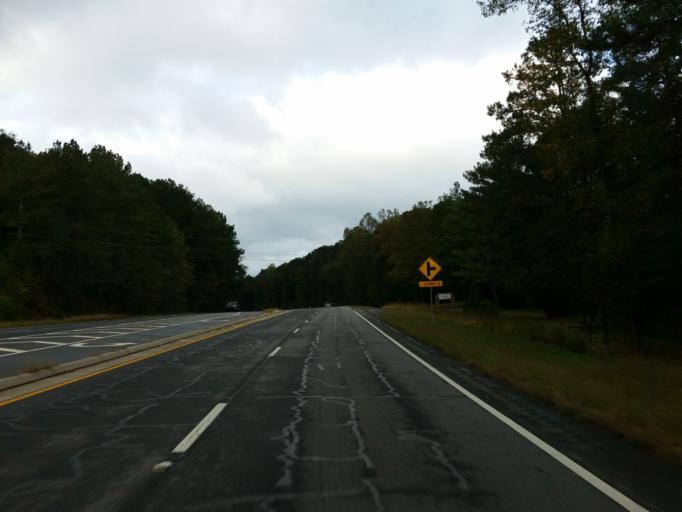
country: US
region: Georgia
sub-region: Bartow County
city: Emerson
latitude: 34.0937
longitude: -84.7402
